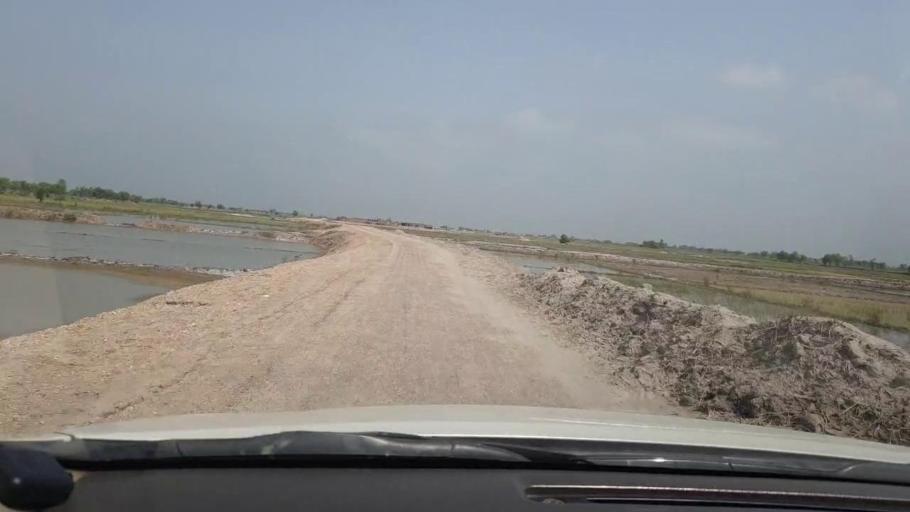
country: PK
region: Sindh
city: Shikarpur
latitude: 27.9982
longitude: 68.5606
